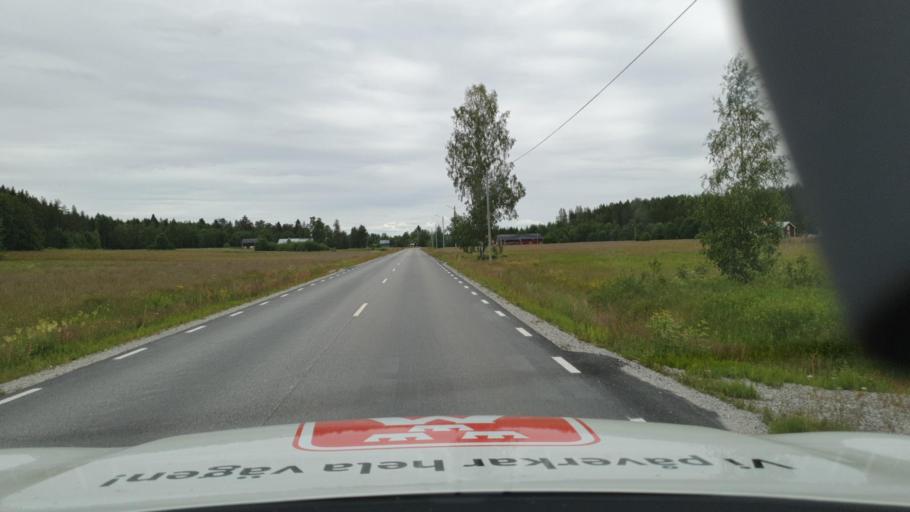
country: SE
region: Vaesterbotten
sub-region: Nordmalings Kommun
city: Nordmaling
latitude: 63.5417
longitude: 19.3699
